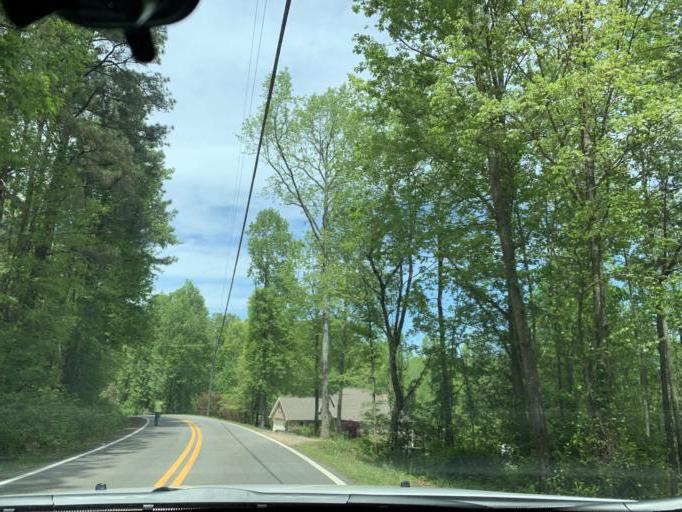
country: US
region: Georgia
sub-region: Hall County
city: Flowery Branch
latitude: 34.2710
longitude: -84.0238
